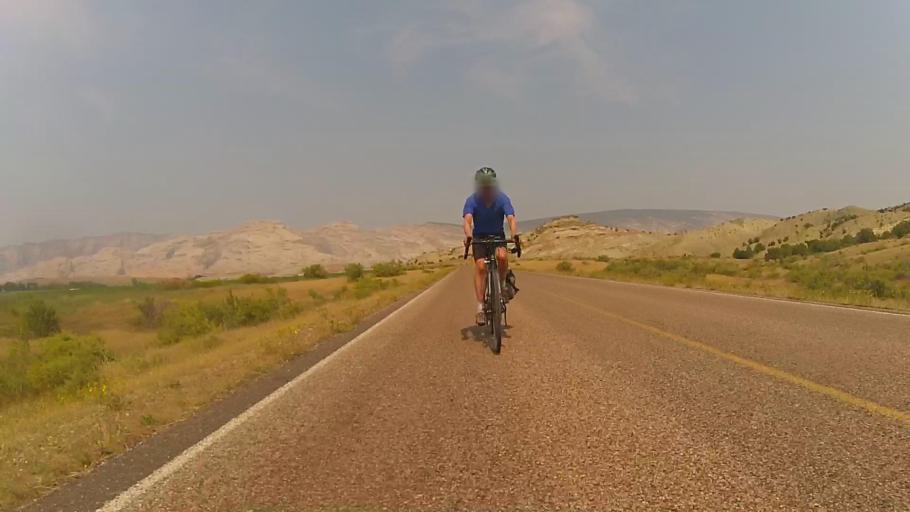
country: US
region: Utah
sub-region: Uintah County
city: Naples
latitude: 40.4110
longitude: -109.2307
